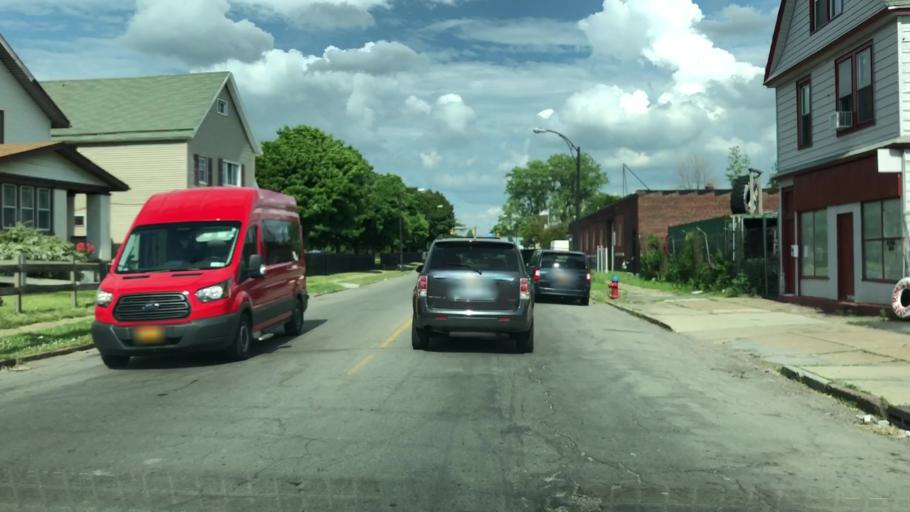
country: US
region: New York
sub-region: Erie County
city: Sloan
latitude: 42.9039
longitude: -78.8211
